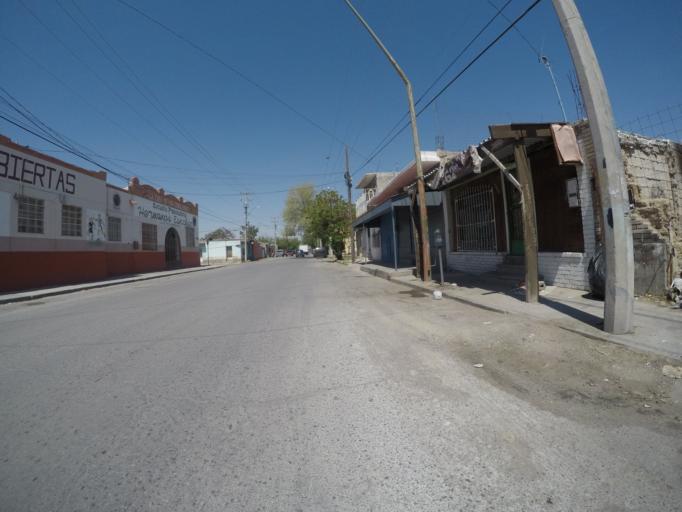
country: MX
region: Chihuahua
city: Ciudad Juarez
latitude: 31.7255
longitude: -106.4796
